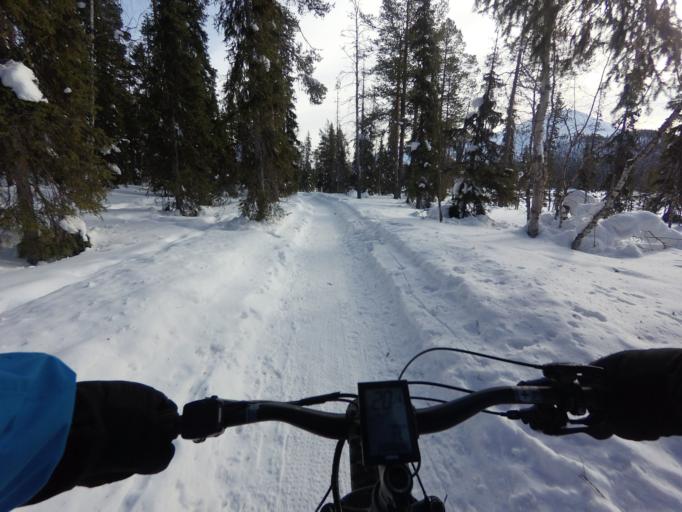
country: FI
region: Lapland
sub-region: Tunturi-Lappi
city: Kolari
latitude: 67.6024
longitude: 24.2292
